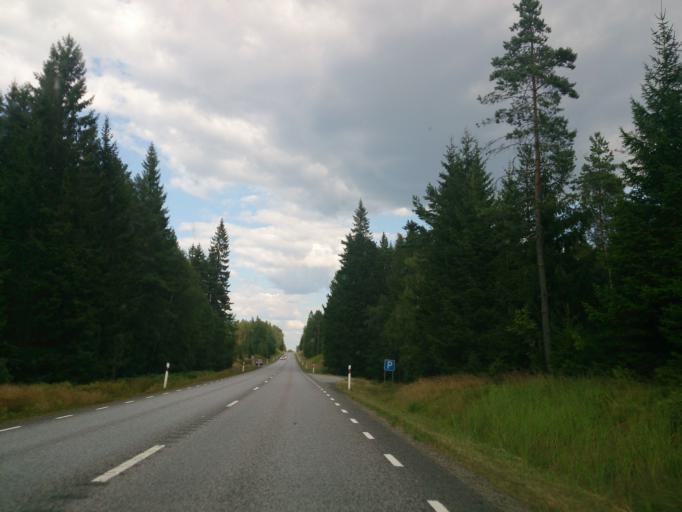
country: SE
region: Joenkoeping
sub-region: Gislaveds Kommun
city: Reftele
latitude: 57.1574
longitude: 13.5408
